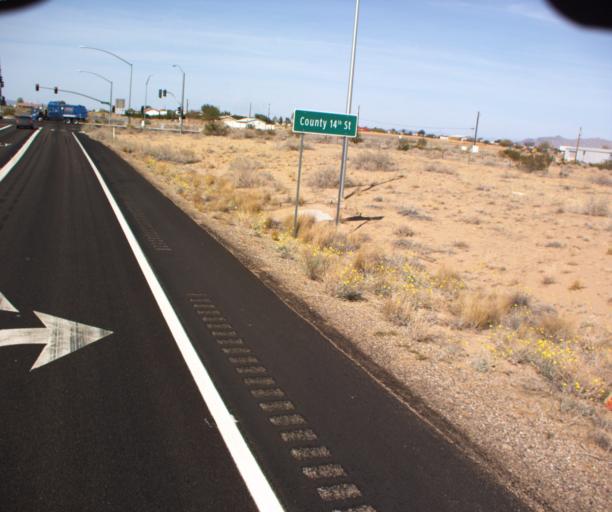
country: US
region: Arizona
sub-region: Yuma County
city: Fortuna Foothills
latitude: 32.6255
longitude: -114.5199
